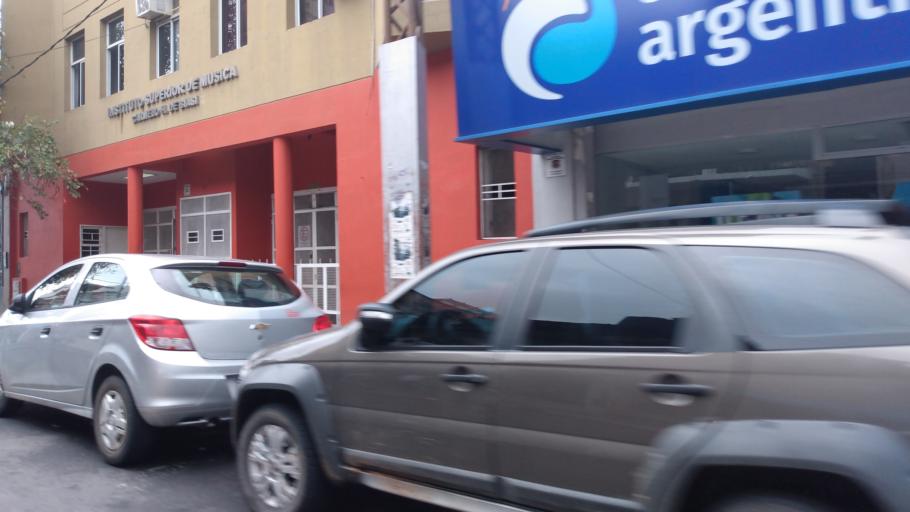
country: AR
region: Corrientes
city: Corrientes
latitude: -27.4675
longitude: -58.8331
